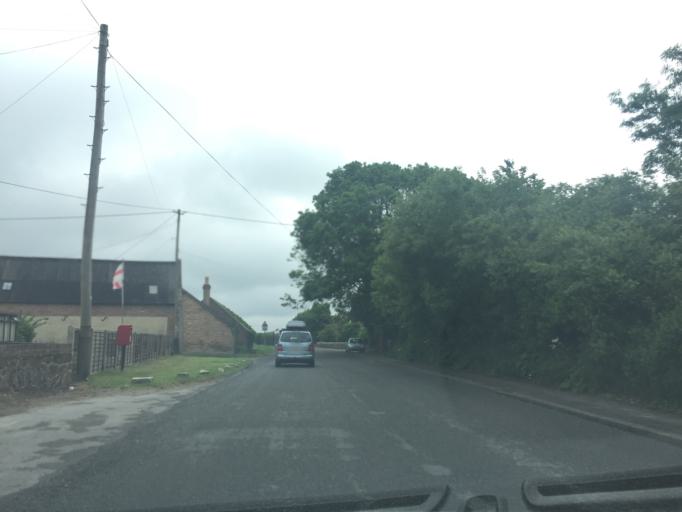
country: GB
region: England
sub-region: Dorset
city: Wool
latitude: 50.6837
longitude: -2.1831
